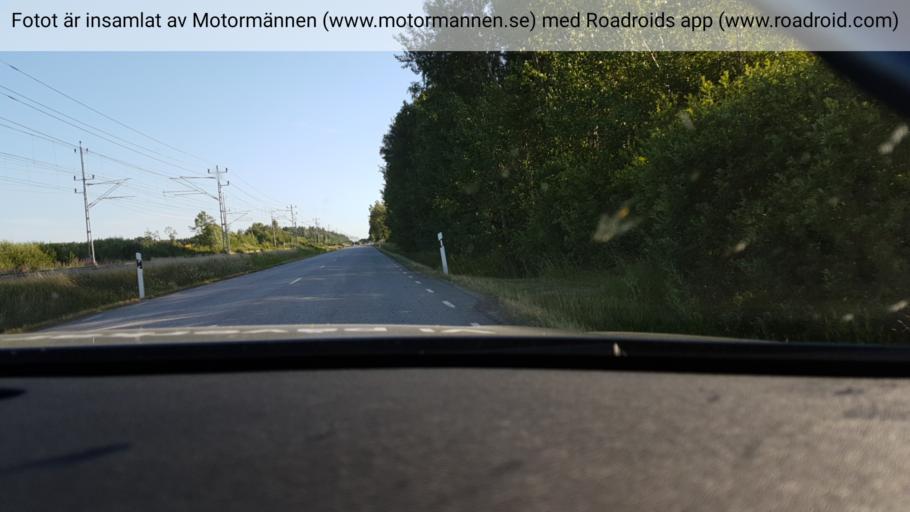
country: SE
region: Vaestra Goetaland
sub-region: Toreboda Kommun
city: Toereboda
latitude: 58.6808
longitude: 14.1071
